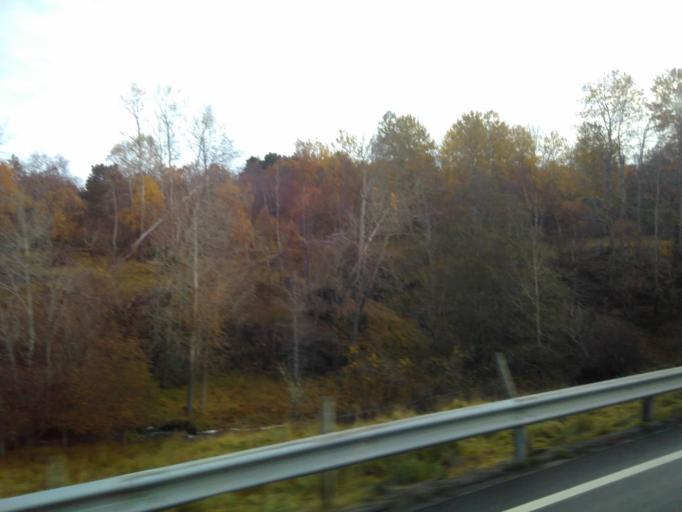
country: NO
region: Sor-Trondelag
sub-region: Hitra
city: Fillan
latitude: 63.5243
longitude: 9.0882
